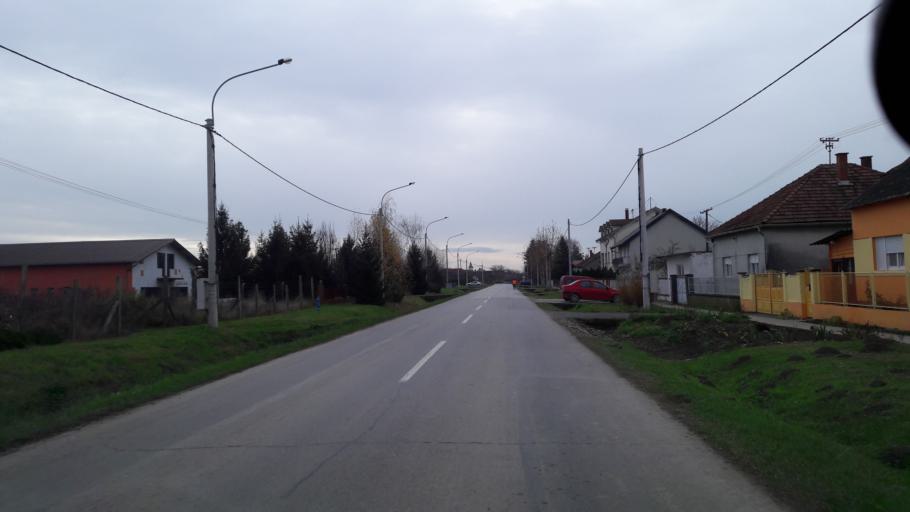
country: HR
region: Osjecko-Baranjska
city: Vladislavci
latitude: 45.4662
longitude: 18.5677
